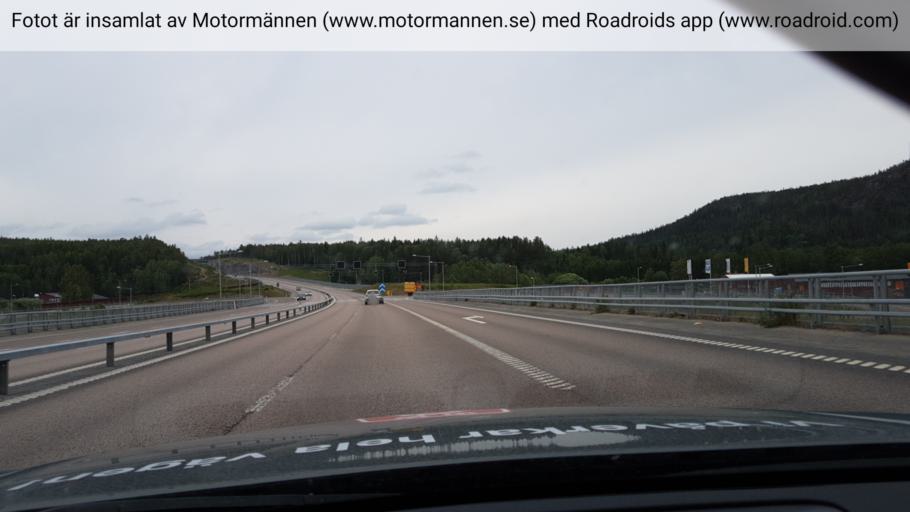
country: SE
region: Vaesternorrland
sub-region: Sundsvalls Kommun
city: Nolby
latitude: 62.2923
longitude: 17.3502
